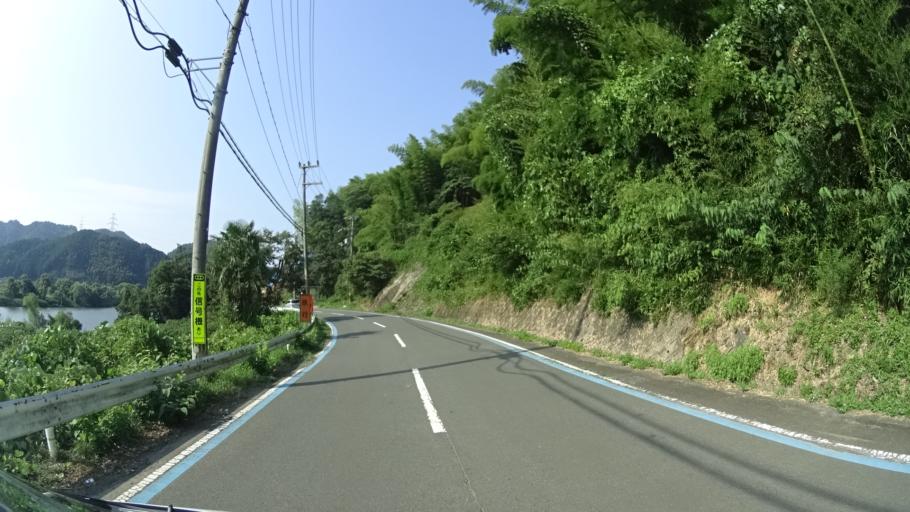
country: JP
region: Kyoto
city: Maizuru
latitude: 35.4348
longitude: 135.2599
